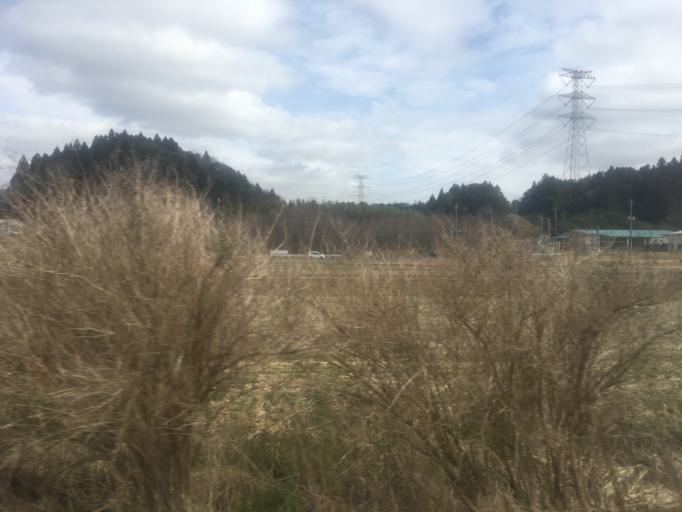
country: JP
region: Chiba
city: Naruto
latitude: 35.6204
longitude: 140.3733
